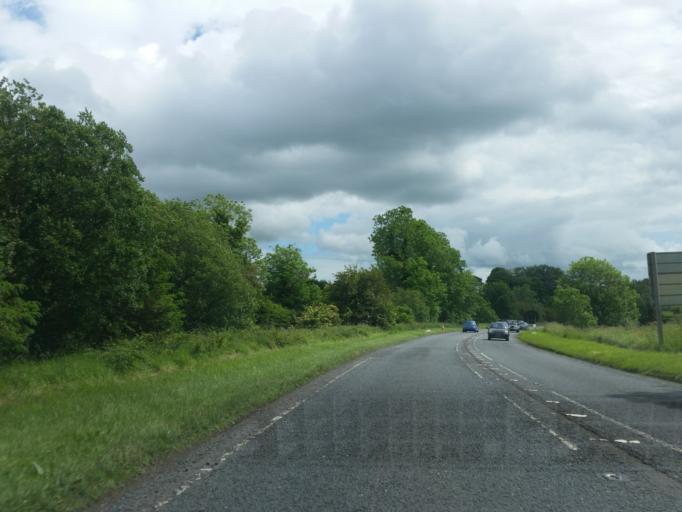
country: IE
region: Ulster
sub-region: County Monaghan
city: Monaghan
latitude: 54.4706
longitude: -7.0496
